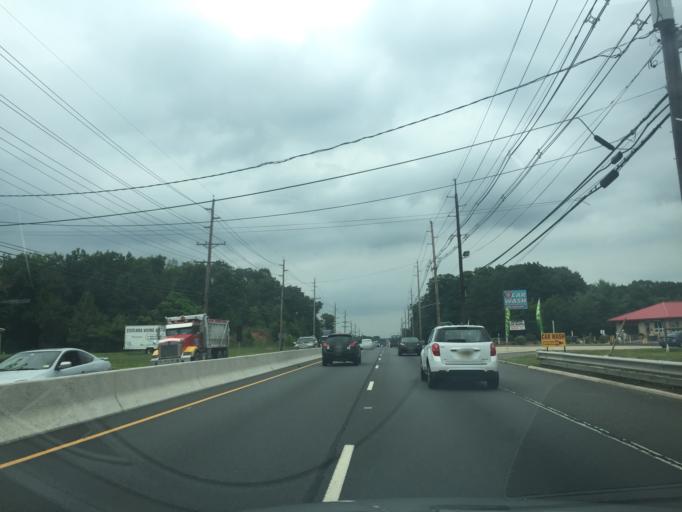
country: US
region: New Jersey
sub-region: Middlesex County
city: Kendall Park
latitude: 40.4077
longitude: -74.5453
